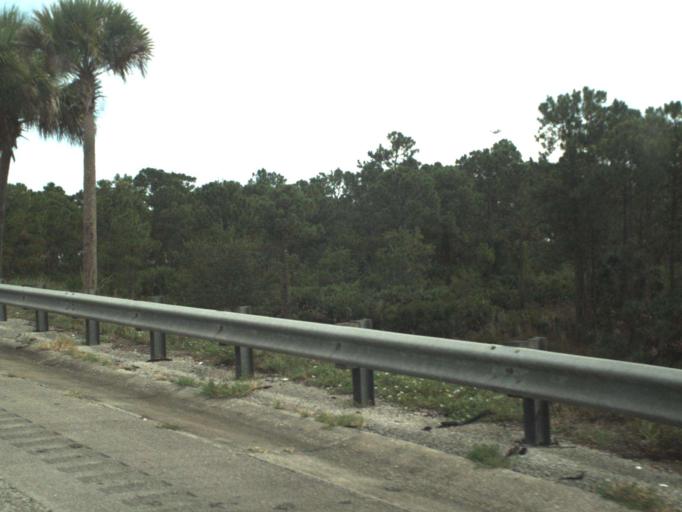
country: US
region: Florida
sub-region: Saint Lucie County
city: Port Saint Lucie
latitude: 27.2621
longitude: -80.4210
